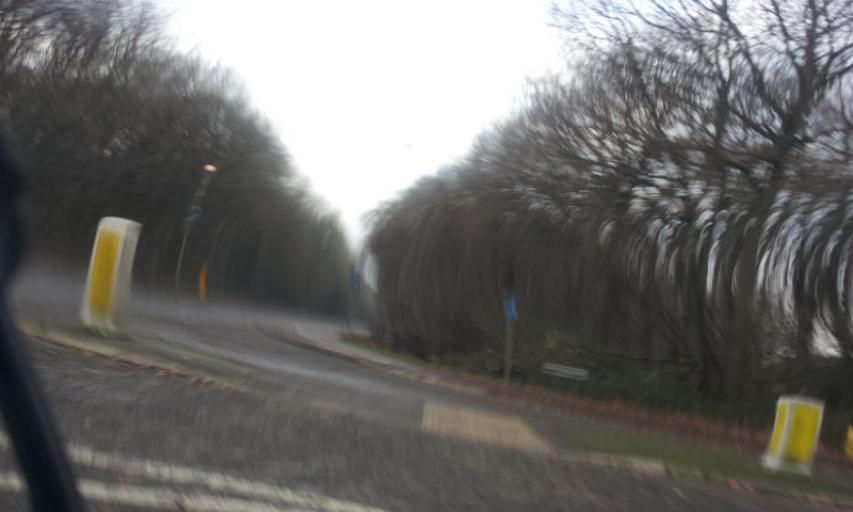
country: GB
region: England
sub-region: Kent
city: Boxley
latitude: 51.3271
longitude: 0.5314
